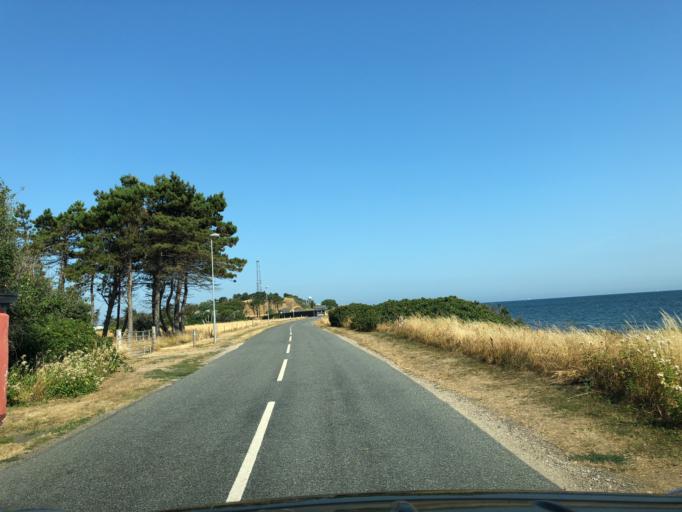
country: DK
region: Zealand
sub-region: Odsherred Kommune
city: Asnaes
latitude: 56.0027
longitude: 11.2854
